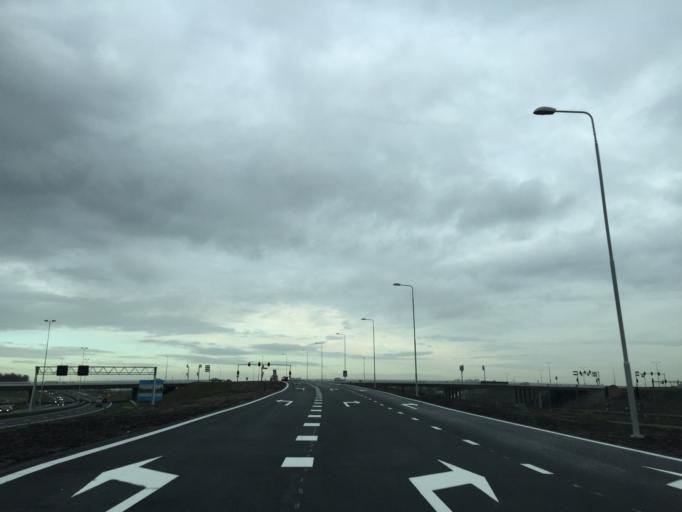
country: NL
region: South Holland
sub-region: Gemeente Waddinxveen
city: Waddinxveen
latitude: 52.0008
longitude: 4.6521
